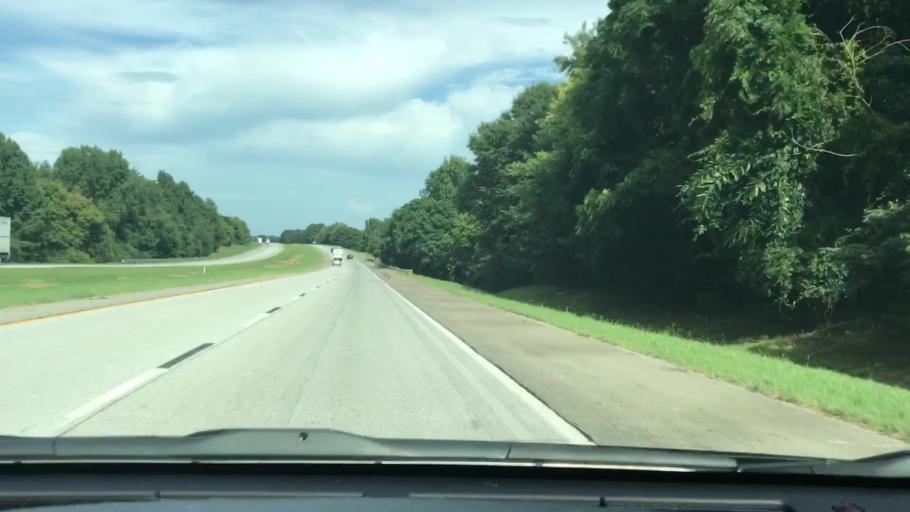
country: US
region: Georgia
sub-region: Morgan County
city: Madison
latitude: 33.5537
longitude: -83.4092
